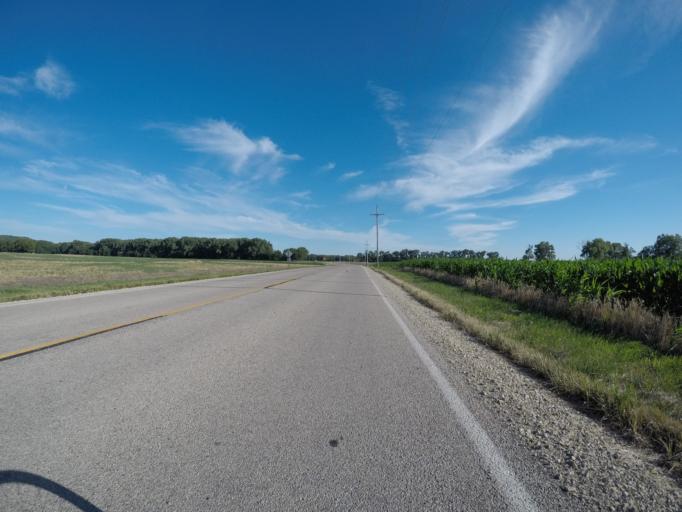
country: US
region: Kansas
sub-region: Riley County
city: Manhattan
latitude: 39.1513
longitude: -96.5812
